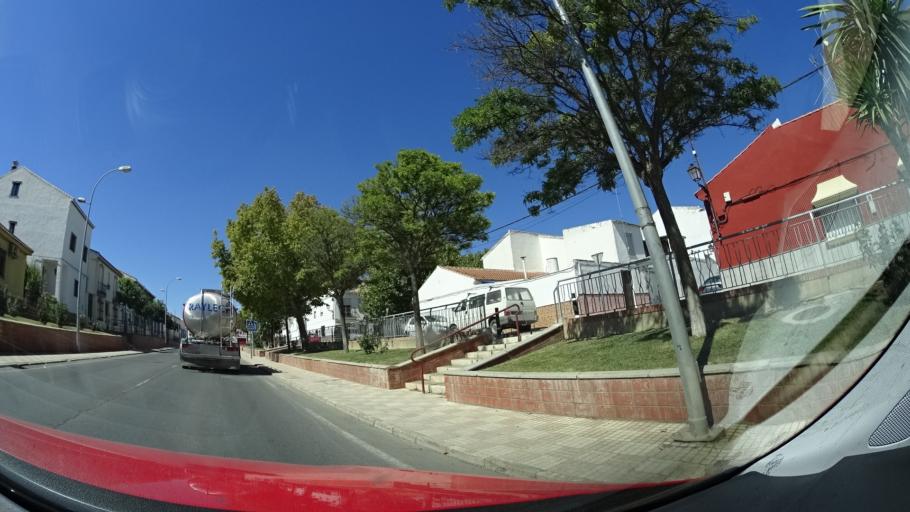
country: ES
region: Andalusia
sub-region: Provincia de Malaga
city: Campillos
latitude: 37.0523
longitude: -4.8611
